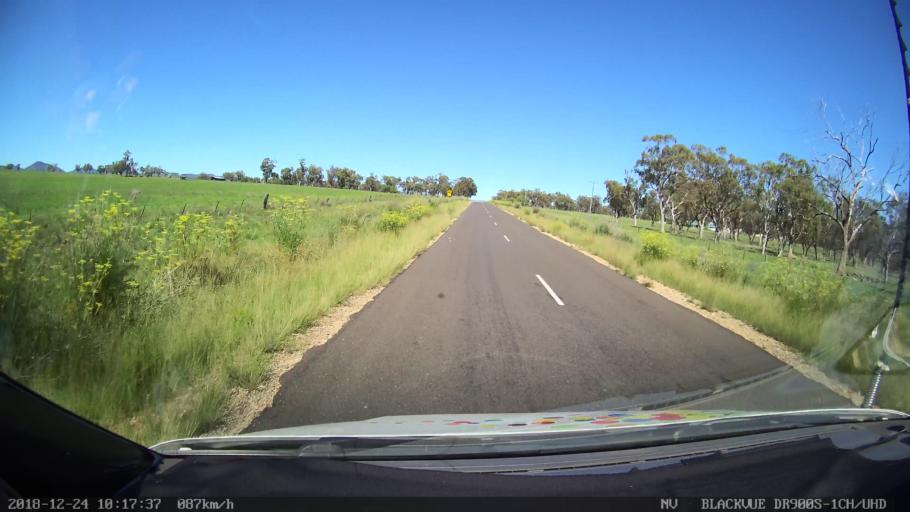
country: AU
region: New South Wales
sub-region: Liverpool Plains
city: Quirindi
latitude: -31.7207
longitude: 150.5887
